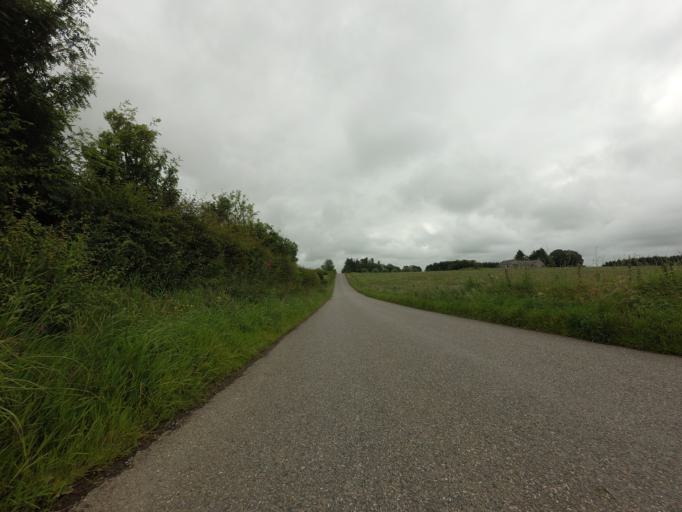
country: GB
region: Scotland
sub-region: Aberdeenshire
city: Mintlaw
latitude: 57.5257
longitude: -2.1431
